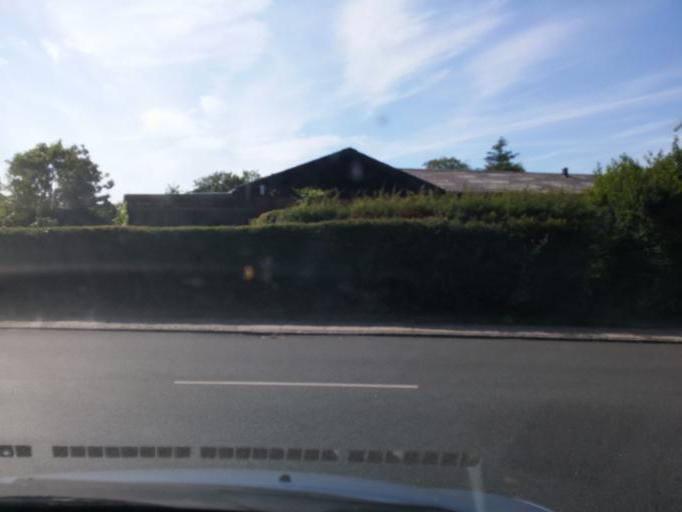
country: DK
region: South Denmark
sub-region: Kerteminde Kommune
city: Munkebo
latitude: 55.4514
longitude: 10.5489
